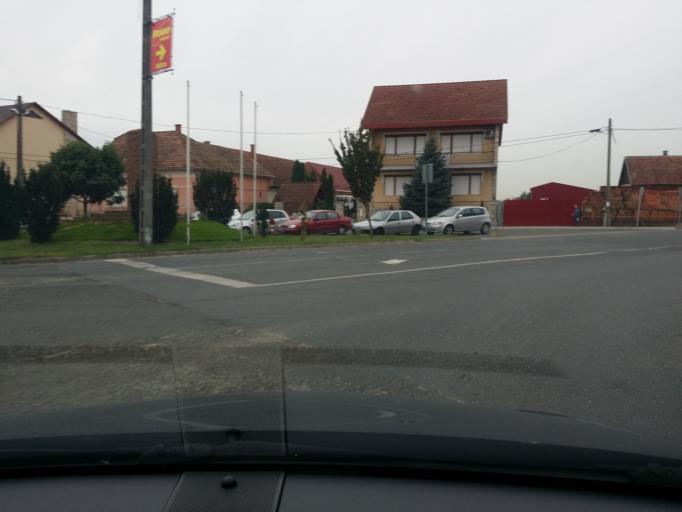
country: HU
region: Pest
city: Alsonemedi
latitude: 47.3155
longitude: 19.1650
